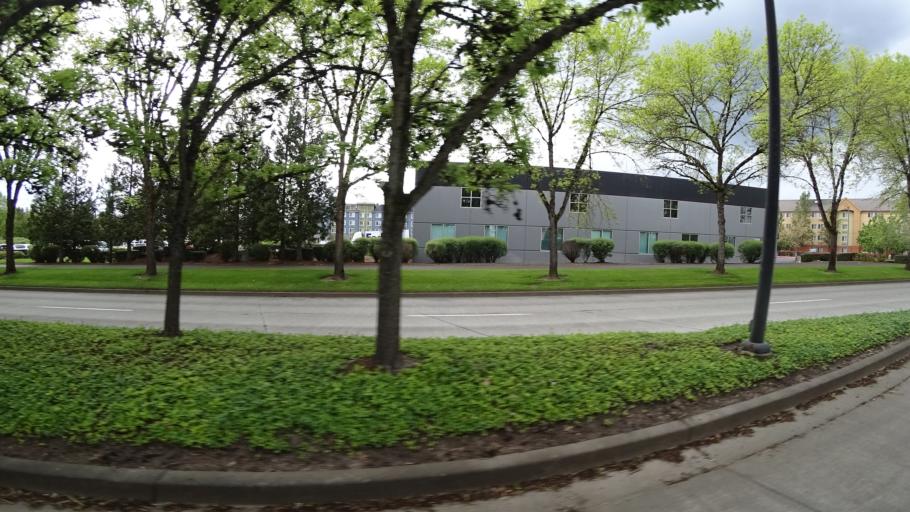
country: US
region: Oregon
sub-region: Washington County
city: Rockcreek
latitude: 45.5463
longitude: -122.9261
